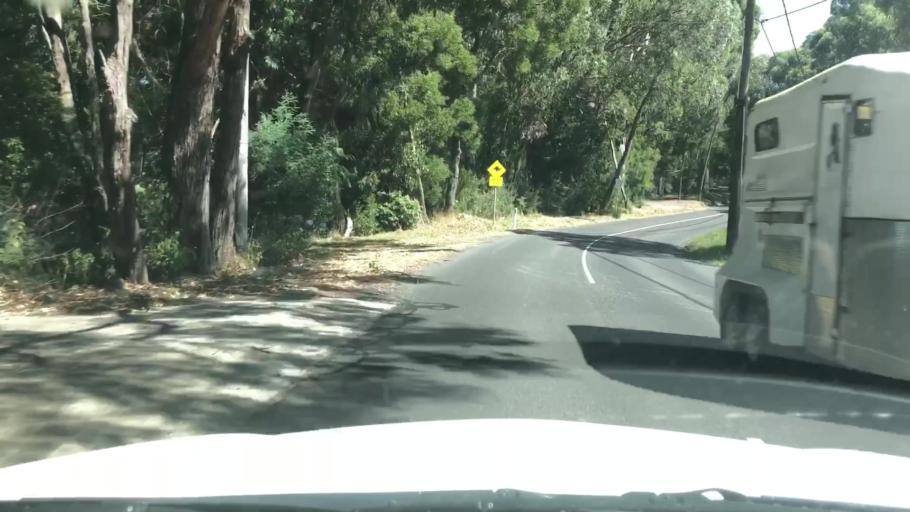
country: AU
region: Victoria
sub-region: Yarra Ranges
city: Macclesfield
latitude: -37.8915
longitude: 145.4756
